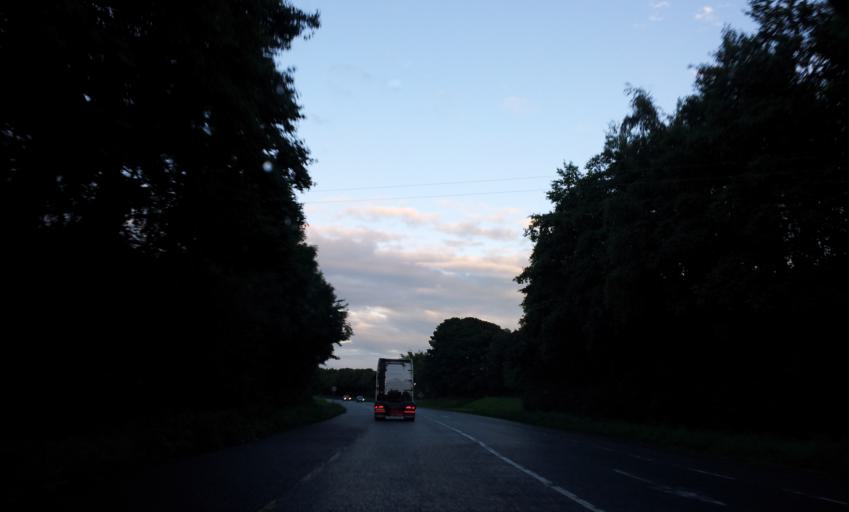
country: IE
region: Munster
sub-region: County Limerick
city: Rathkeale
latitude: 52.5287
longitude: -8.8969
